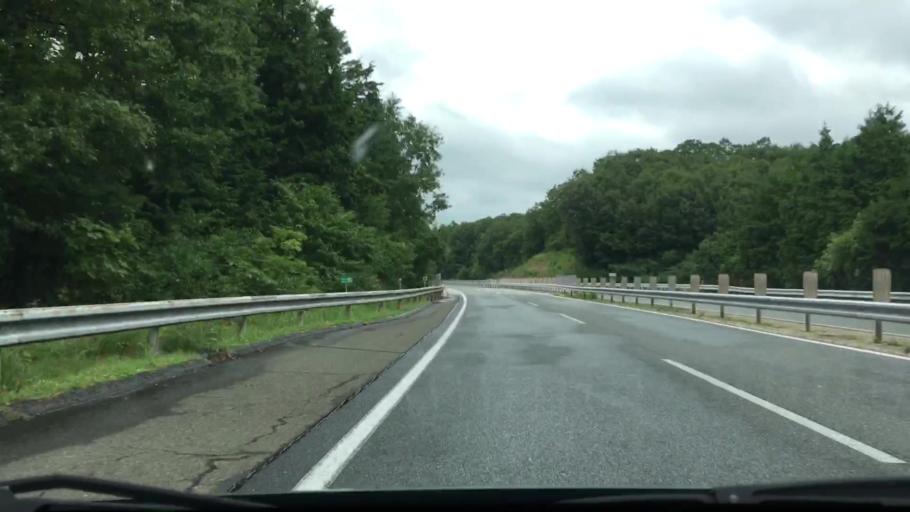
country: JP
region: Hiroshima
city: Shobara
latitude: 34.8401
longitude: 133.0422
